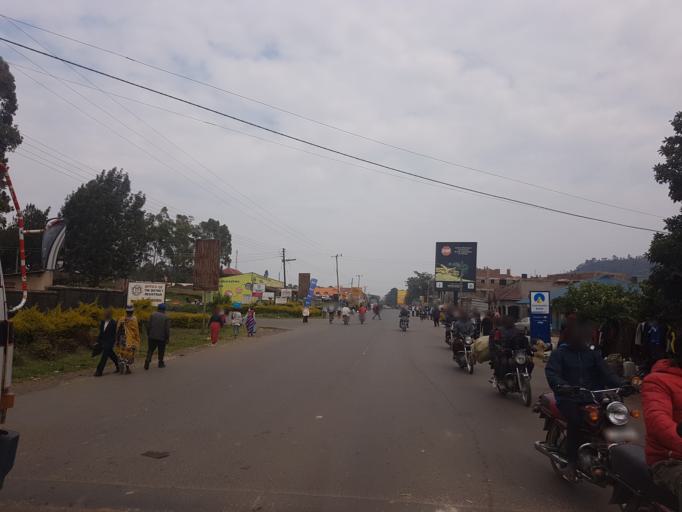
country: UG
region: Western Region
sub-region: Kisoro District
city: Kisoro
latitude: -1.2826
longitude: 29.6988
